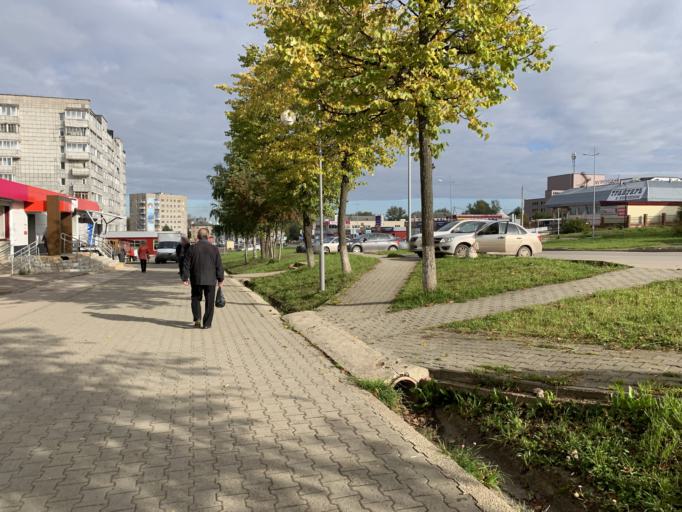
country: RU
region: Perm
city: Gubakha
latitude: 58.8349
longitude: 57.5552
